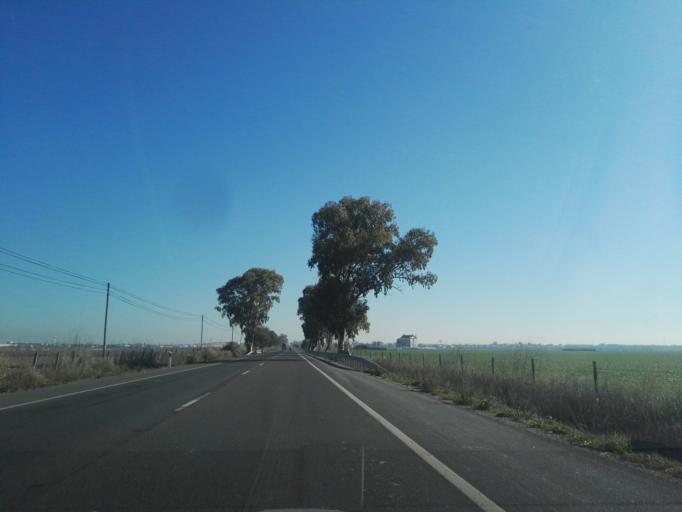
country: PT
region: Santarem
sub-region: Benavente
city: Samora Correia
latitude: 38.9305
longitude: -8.9094
